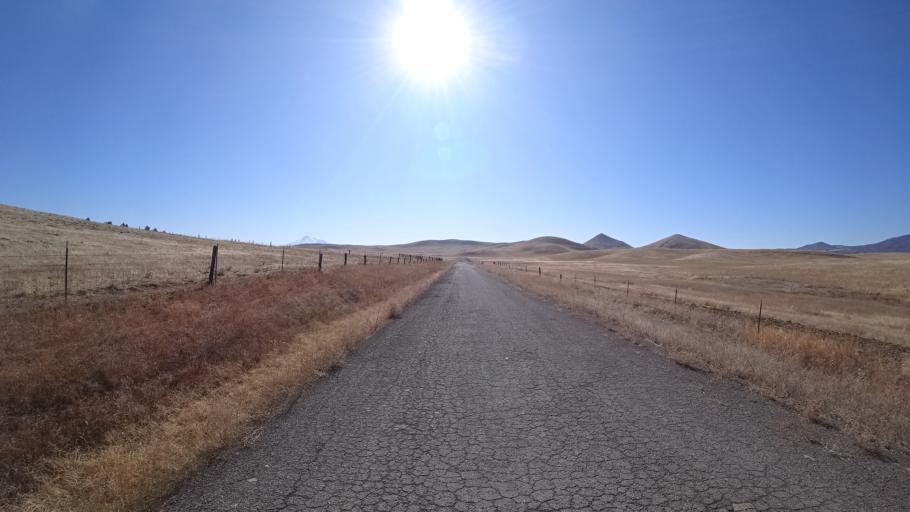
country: US
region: California
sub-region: Siskiyou County
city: Montague
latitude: 41.8454
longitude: -122.4595
